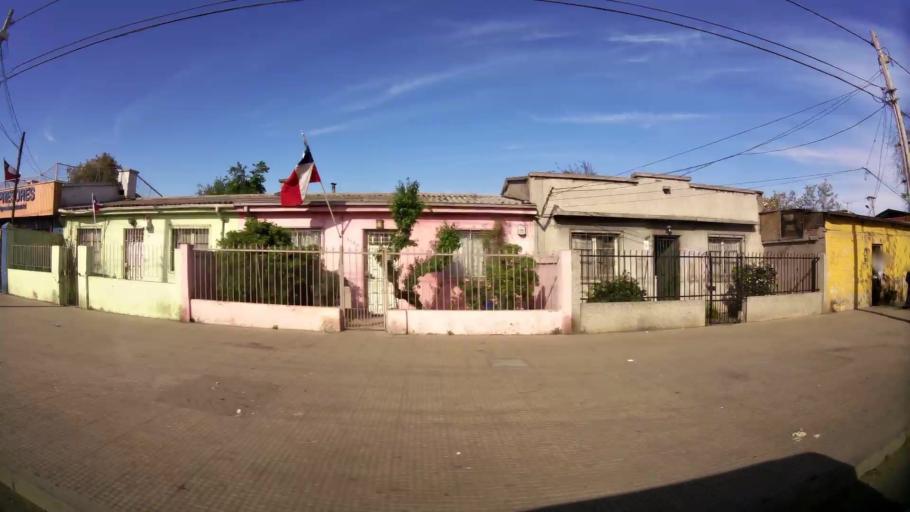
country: CL
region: Santiago Metropolitan
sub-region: Provincia de Santiago
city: Santiago
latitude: -33.4638
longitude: -70.6880
